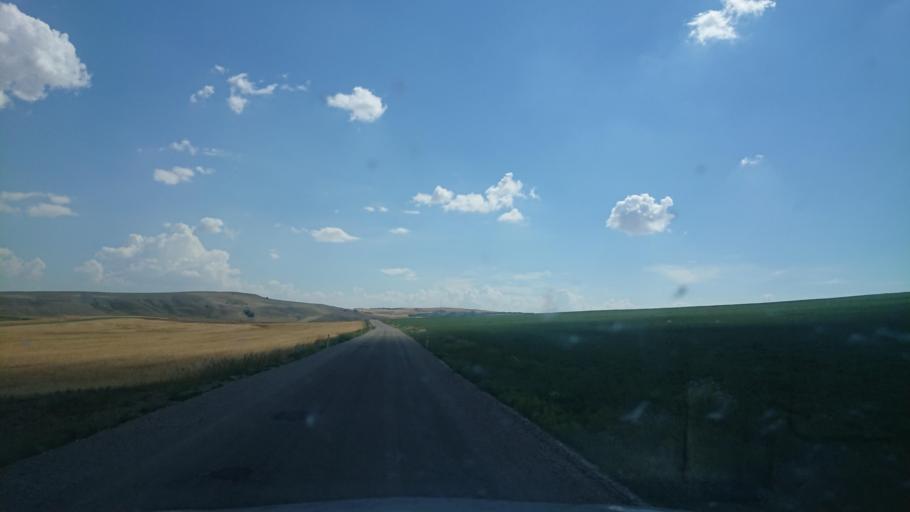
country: TR
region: Aksaray
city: Agacoren
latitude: 38.7904
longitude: 33.8135
